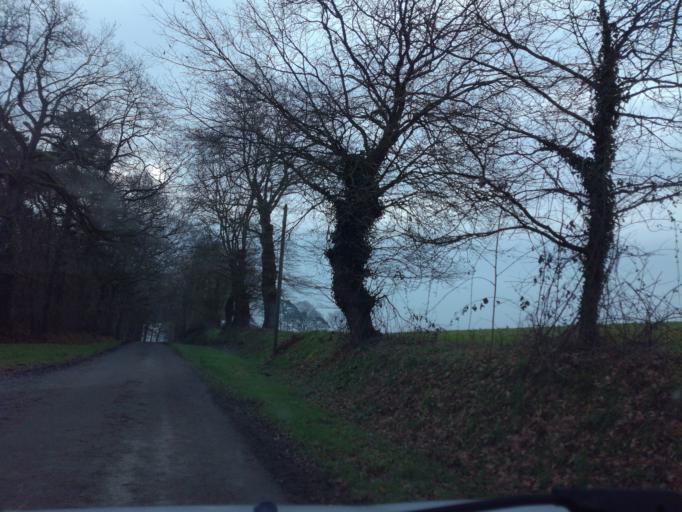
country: FR
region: Brittany
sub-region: Departement d'Ille-et-Vilaine
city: Gosne
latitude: 48.2644
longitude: -1.4748
